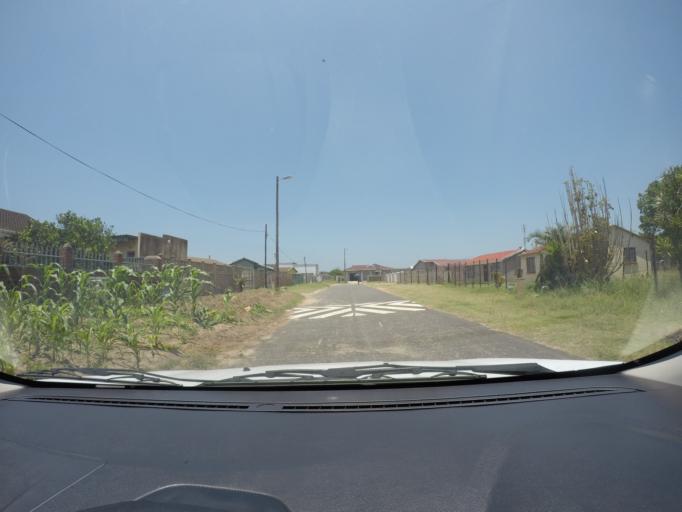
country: ZA
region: KwaZulu-Natal
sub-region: uThungulu District Municipality
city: eSikhawini
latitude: -28.8808
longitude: 31.9023
